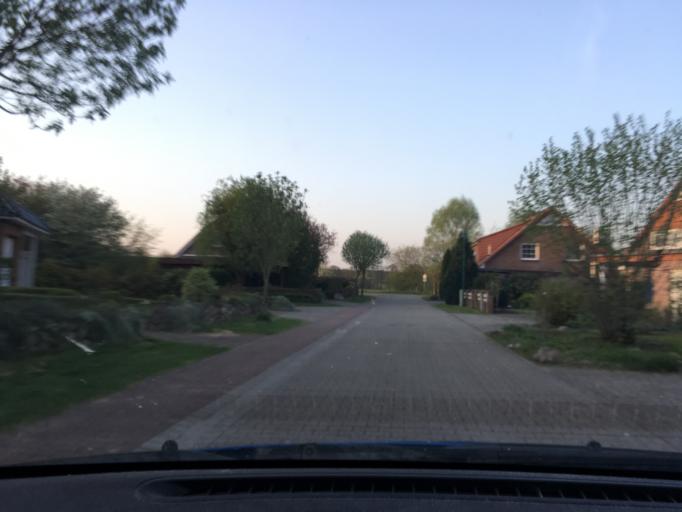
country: DE
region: Lower Saxony
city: Kirchgellersen
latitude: 53.2341
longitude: 10.2980
